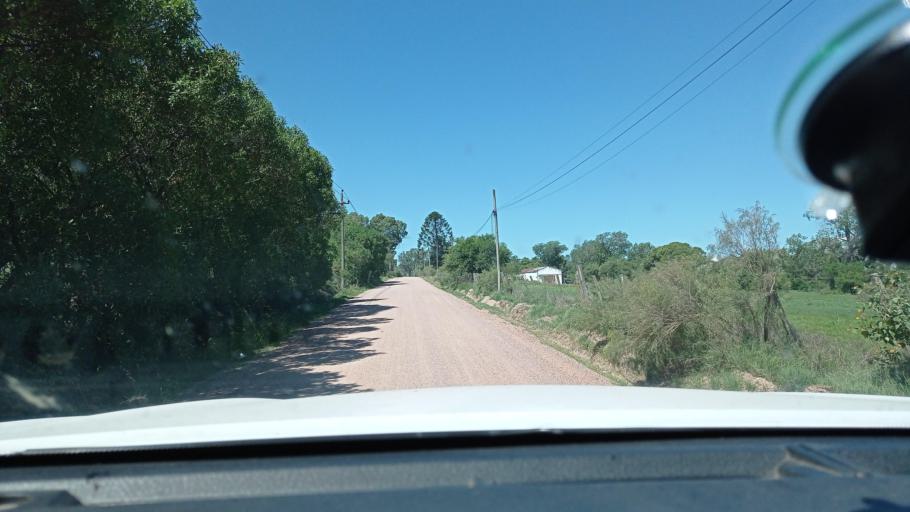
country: UY
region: Canelones
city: La Paz
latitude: -34.7601
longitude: -56.1760
